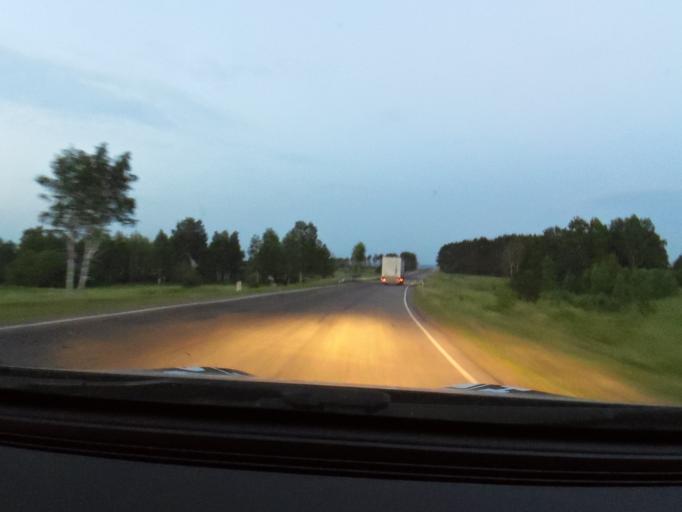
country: RU
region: Bashkortostan
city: Duvan
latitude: 56.0756
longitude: 58.1512
